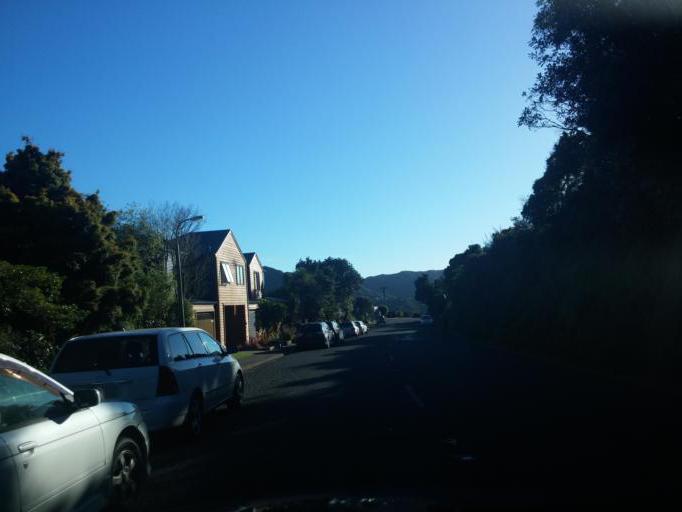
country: NZ
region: Wellington
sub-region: Wellington City
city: Kelburn
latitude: -41.2698
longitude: 174.7636
